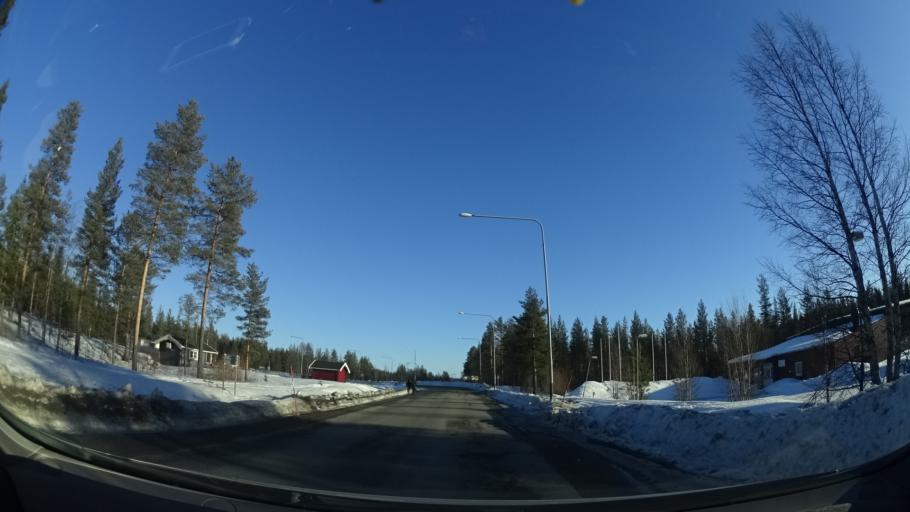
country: SE
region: Vaesterbotten
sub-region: Skelleftea Kommun
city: Langsele
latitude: 65.0540
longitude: 20.0550
